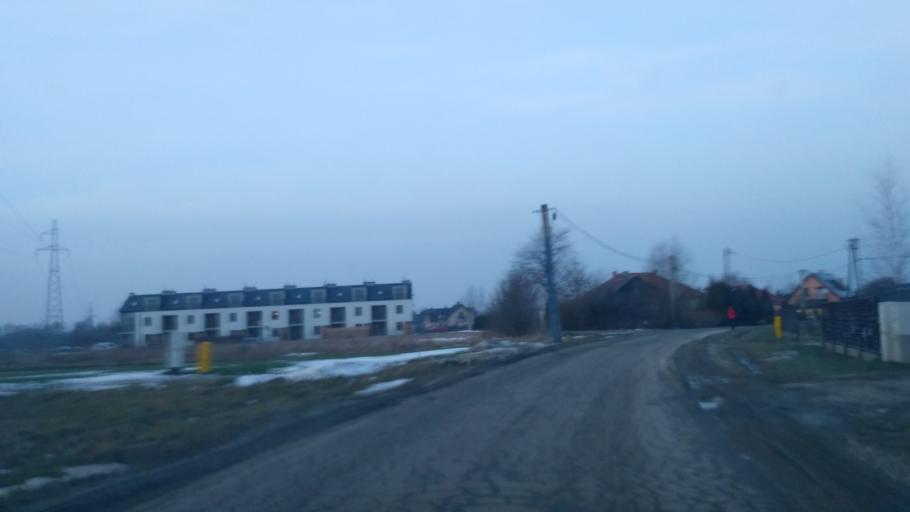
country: PL
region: Subcarpathian Voivodeship
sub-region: Powiat rzeszowski
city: Boguchwala
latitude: 49.9865
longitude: 21.9724
